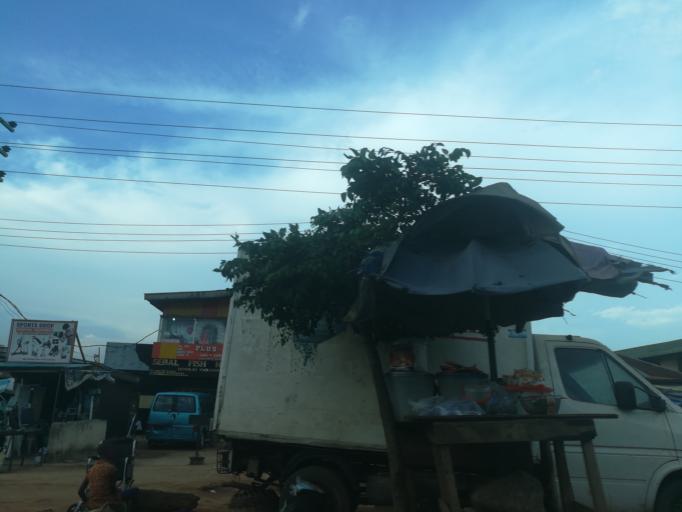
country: NG
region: Lagos
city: Ikorodu
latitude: 6.6240
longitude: 3.4956
